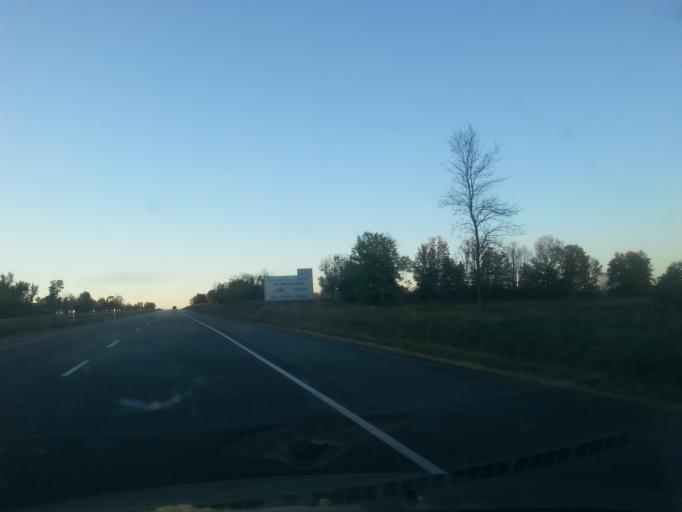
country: CA
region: Ontario
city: Barrie
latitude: 44.4374
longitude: -79.6609
